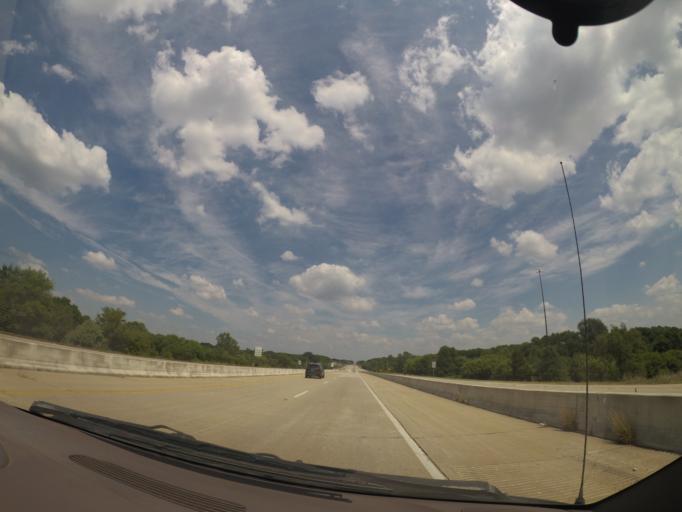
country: US
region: Indiana
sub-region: Elkhart County
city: Dunlap
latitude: 41.6668
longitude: -85.8858
